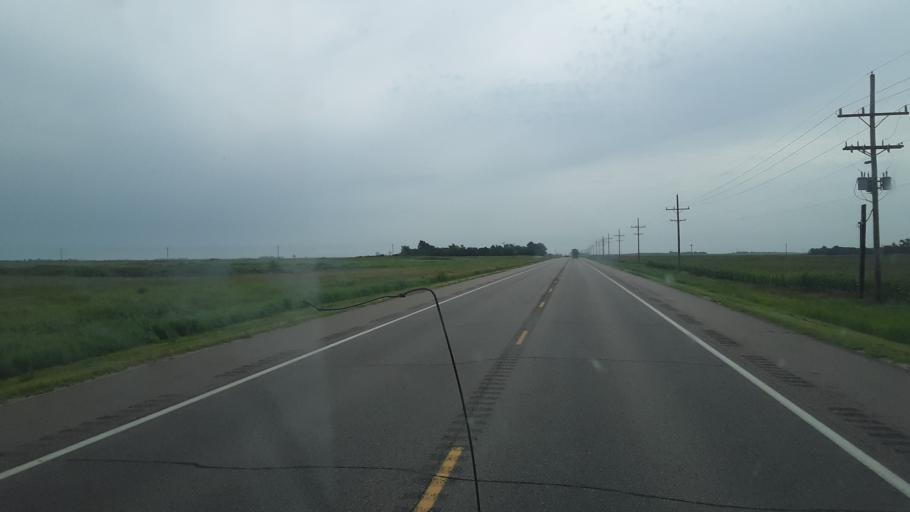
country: US
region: Kansas
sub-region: Edwards County
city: Kinsley
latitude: 37.9275
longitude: -99.3198
